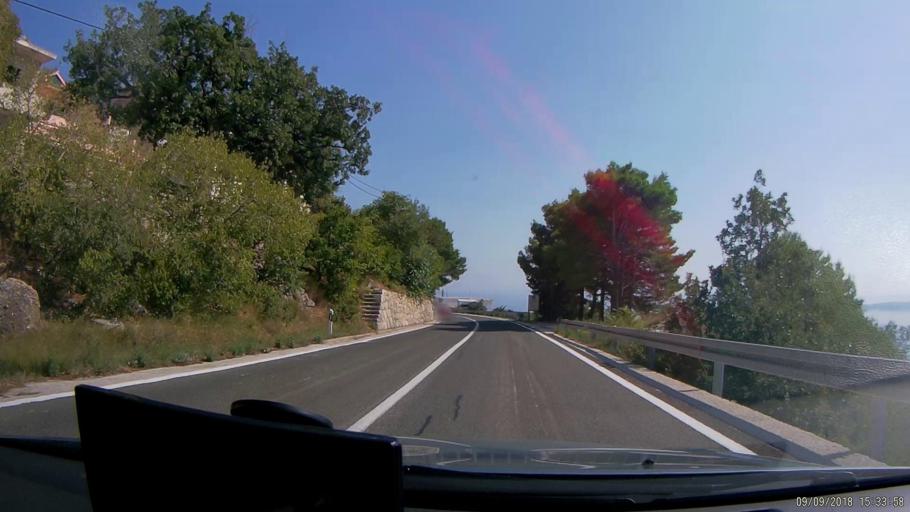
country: HR
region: Splitsko-Dalmatinska
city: Donja Brela
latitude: 43.3901
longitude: 16.9010
